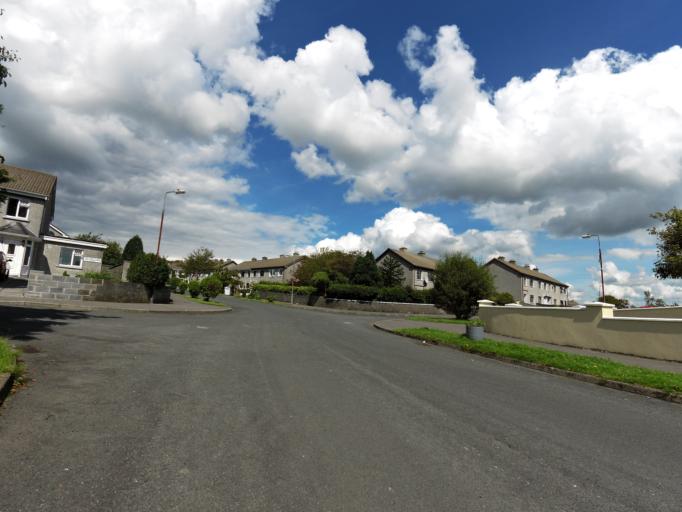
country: IE
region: Connaught
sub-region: County Galway
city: Gaillimh
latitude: 53.2791
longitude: -9.0760
